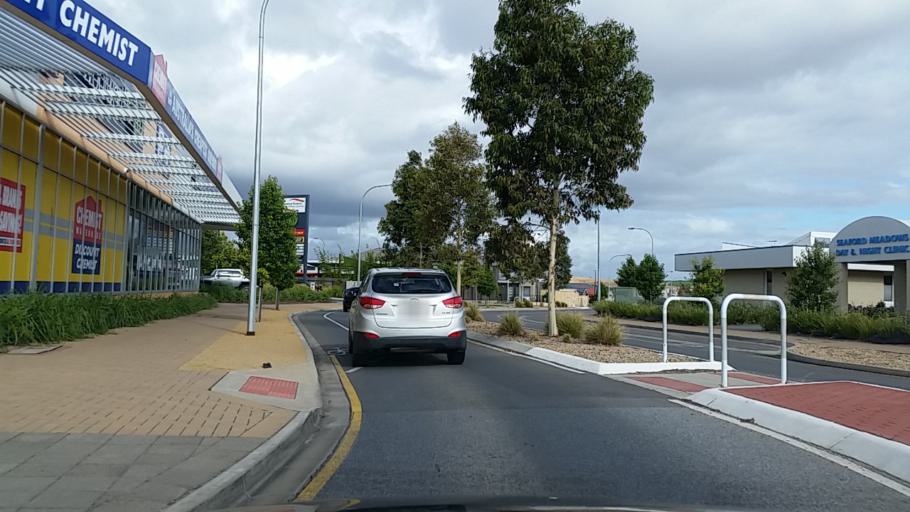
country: AU
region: South Australia
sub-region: Onkaparinga
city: Seaford
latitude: -35.1730
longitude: 138.4827
